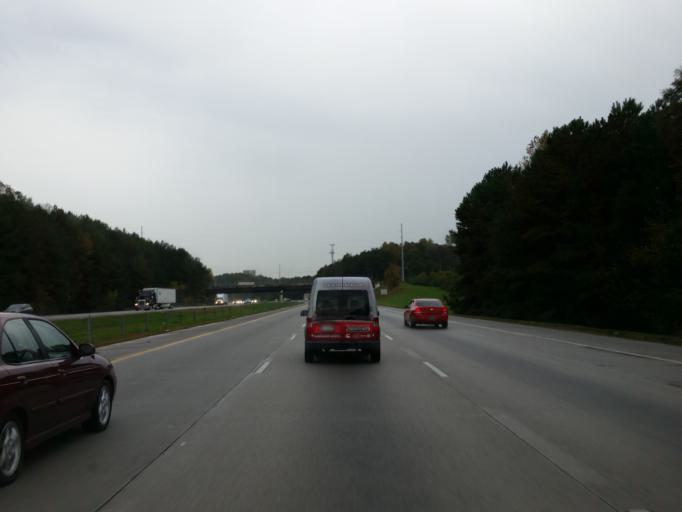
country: US
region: Georgia
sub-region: Clayton County
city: Conley
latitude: 33.6604
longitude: -84.3252
